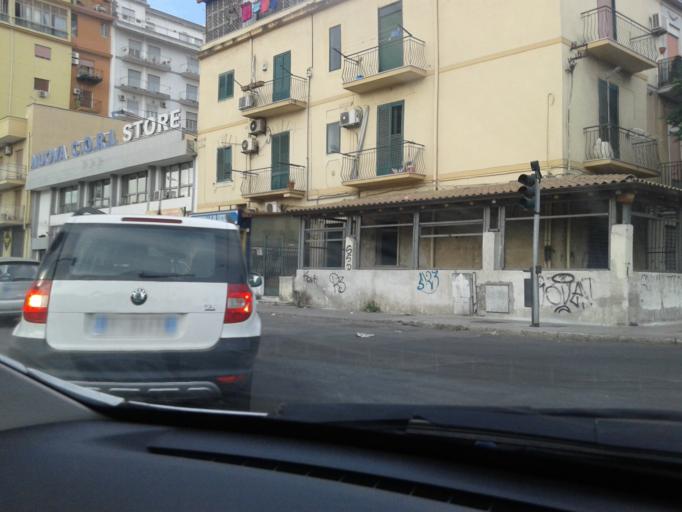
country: IT
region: Sicily
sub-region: Palermo
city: Palermo
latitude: 38.1105
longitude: 13.3296
